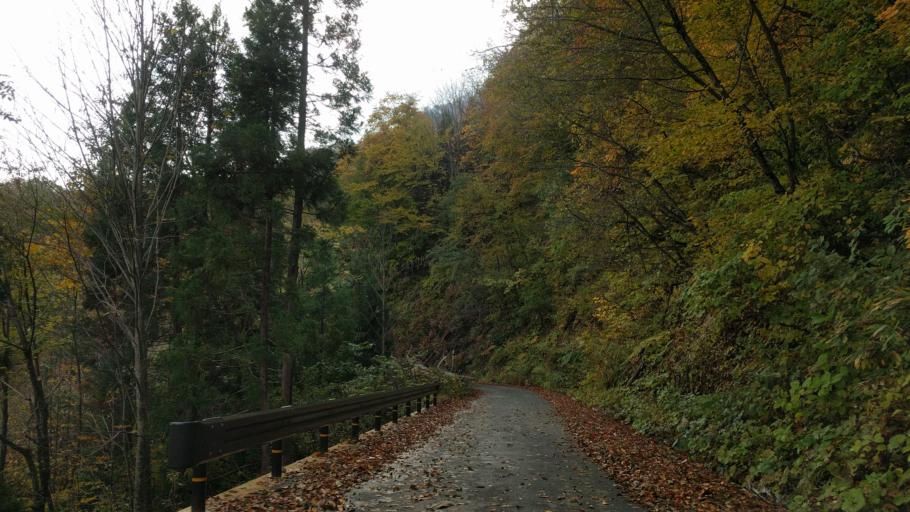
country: JP
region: Fukushima
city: Kitakata
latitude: 37.3799
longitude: 139.6935
